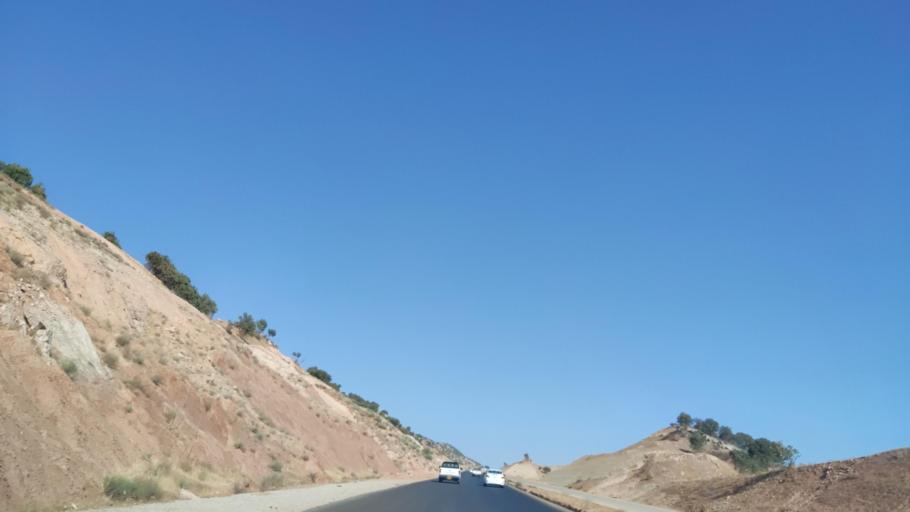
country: IQ
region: Arbil
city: Shaqlawah
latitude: 36.4354
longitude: 44.2952
